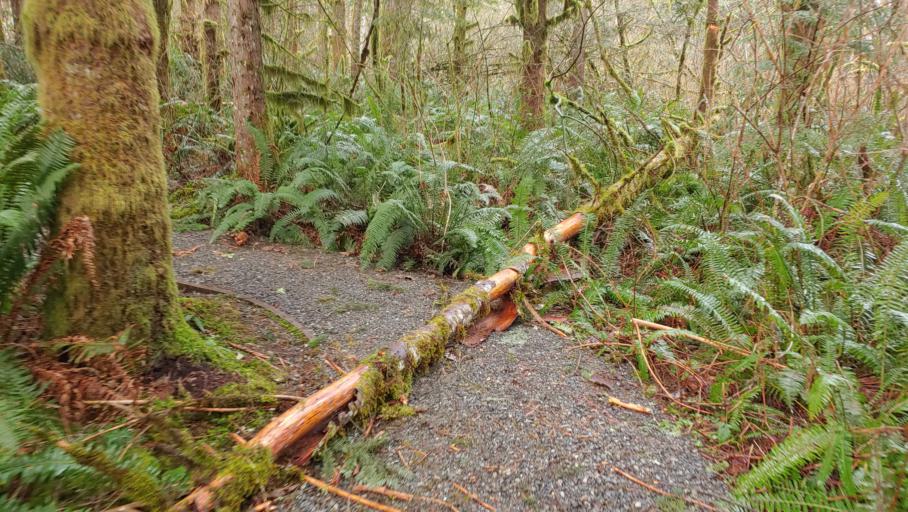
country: US
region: Washington
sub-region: King County
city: Hobart
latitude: 47.4677
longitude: -121.9354
